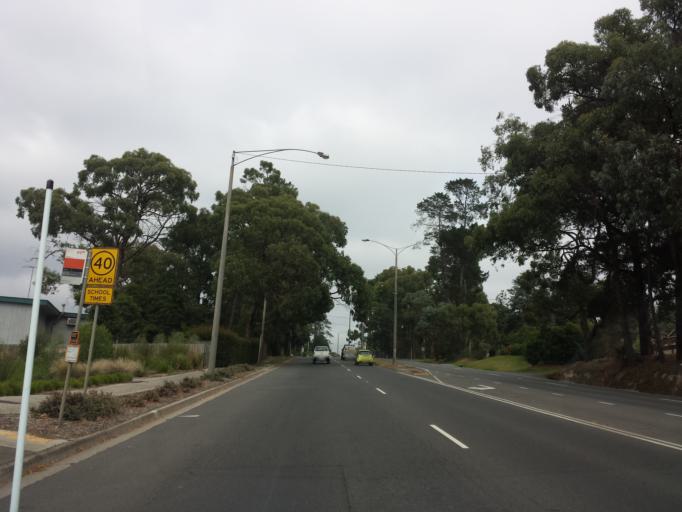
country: AU
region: Victoria
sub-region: Yarra Ranges
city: Montrose
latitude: -37.8084
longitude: 145.3466
